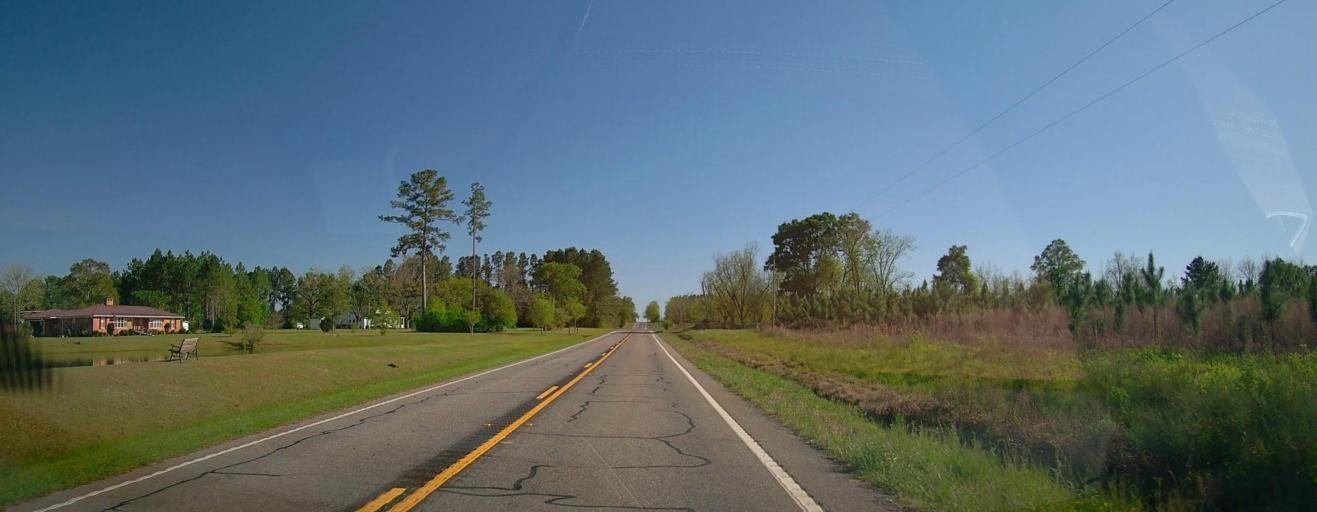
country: US
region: Georgia
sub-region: Wilcox County
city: Rochelle
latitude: 31.8310
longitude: -83.4890
